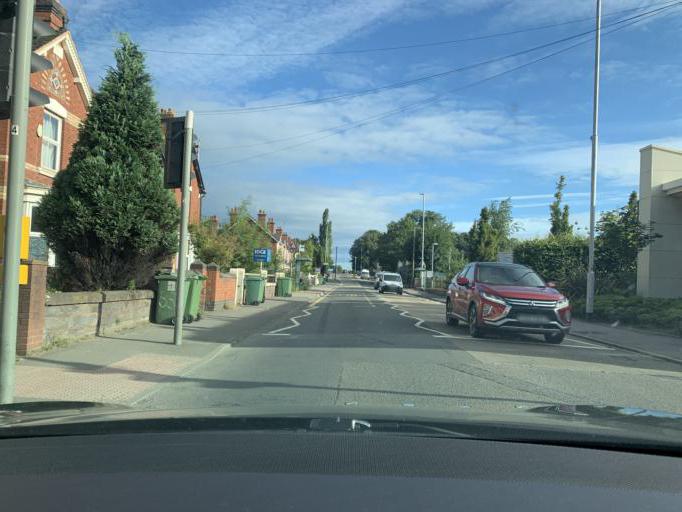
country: GB
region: England
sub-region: Staffordshire
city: Stafford
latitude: 52.8171
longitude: -2.1238
